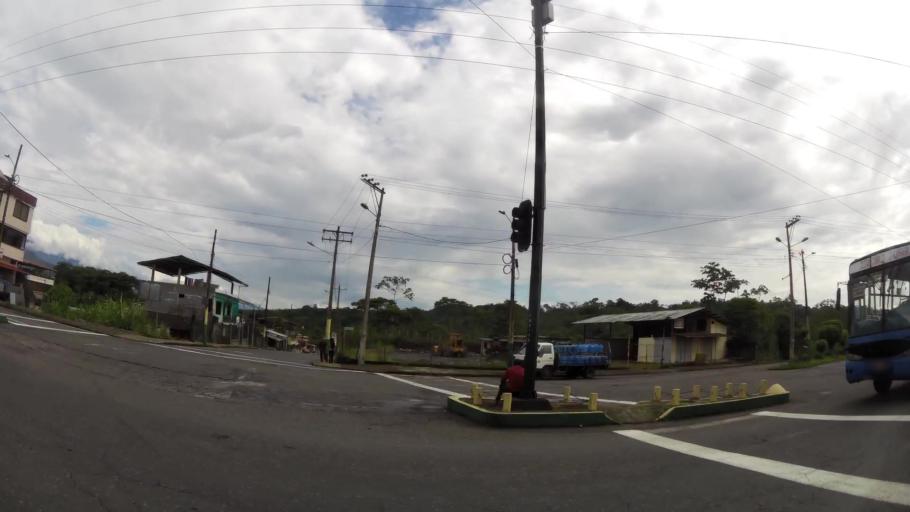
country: EC
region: Pastaza
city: Puyo
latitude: -1.4914
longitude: -77.9911
